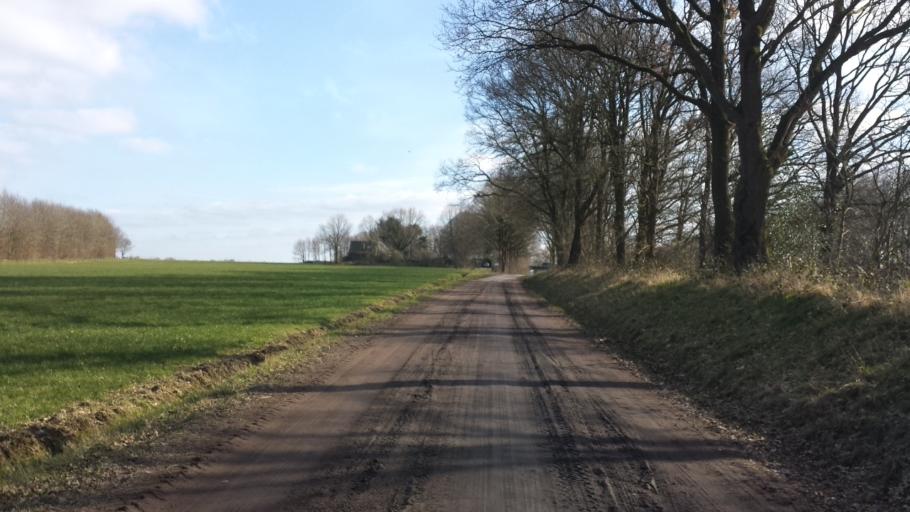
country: NL
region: Overijssel
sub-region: Gemeente Steenwijkerland
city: Tuk
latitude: 52.8066
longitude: 6.0892
